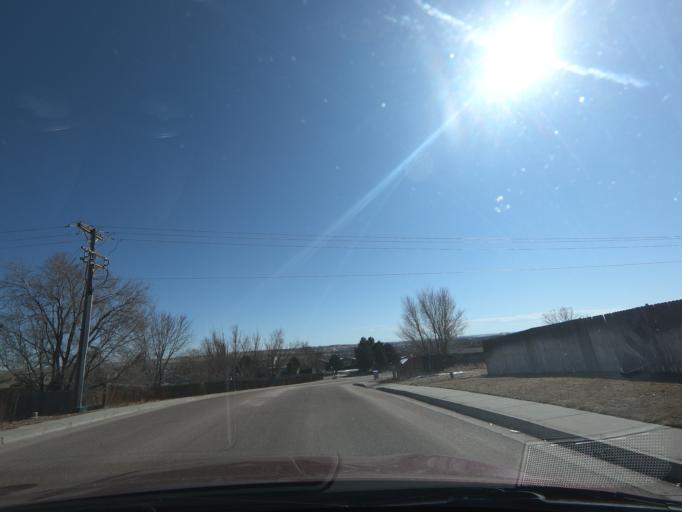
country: US
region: Colorado
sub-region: El Paso County
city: Security-Widefield
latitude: 38.7229
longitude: -104.6899
